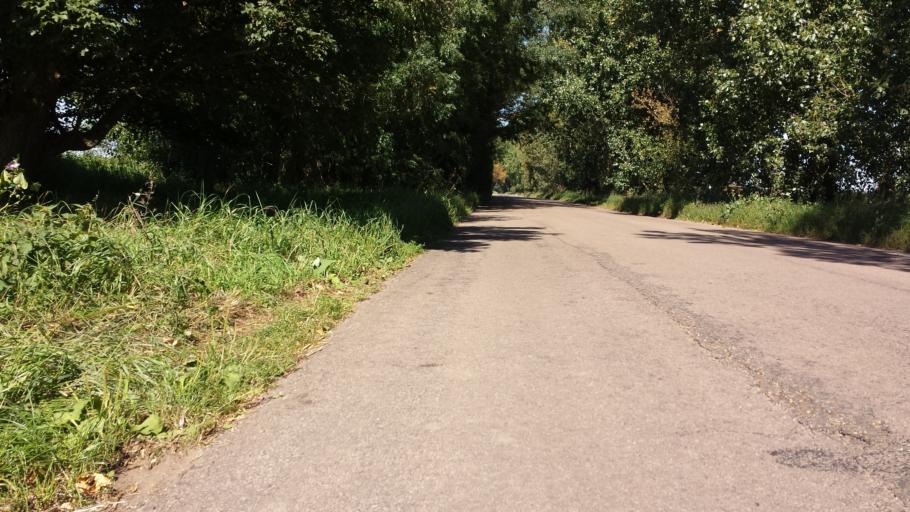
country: GB
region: England
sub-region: Cambridgeshire
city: Isleham
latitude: 52.3450
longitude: 0.3815
